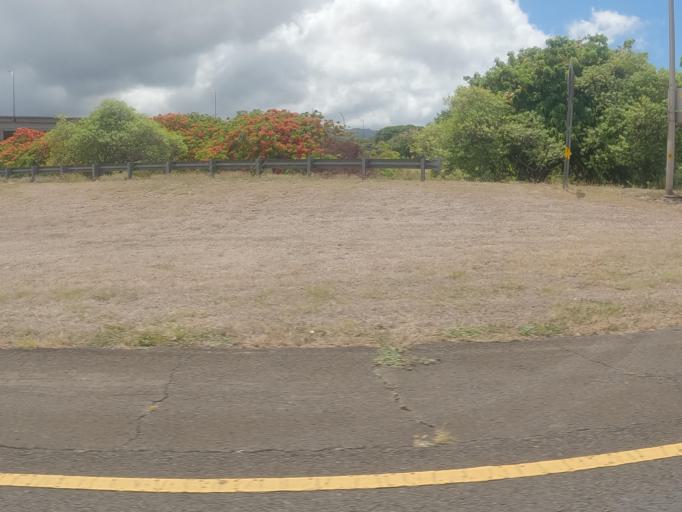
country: US
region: Hawaii
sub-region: Honolulu County
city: Halawa
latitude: 21.3705
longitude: -157.9274
